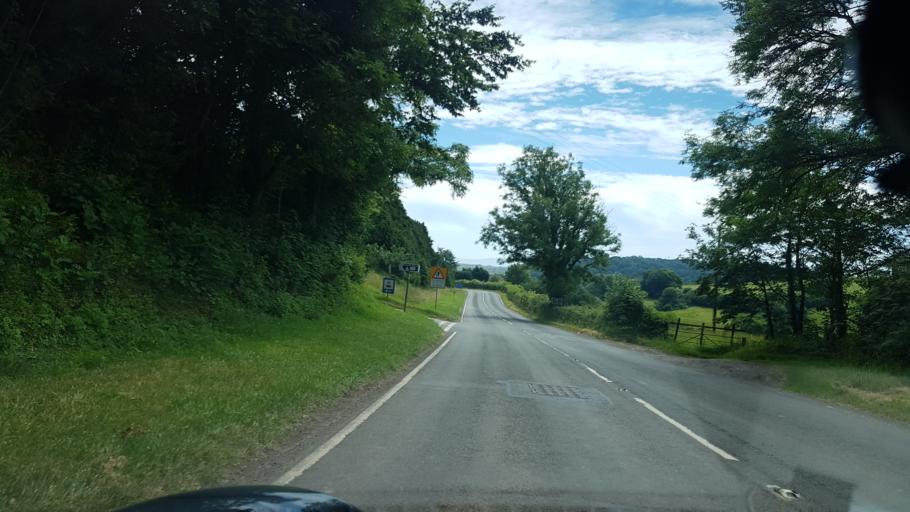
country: GB
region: Wales
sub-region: Carmarthenshire
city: Saint Clears
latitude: 51.7793
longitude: -4.4698
